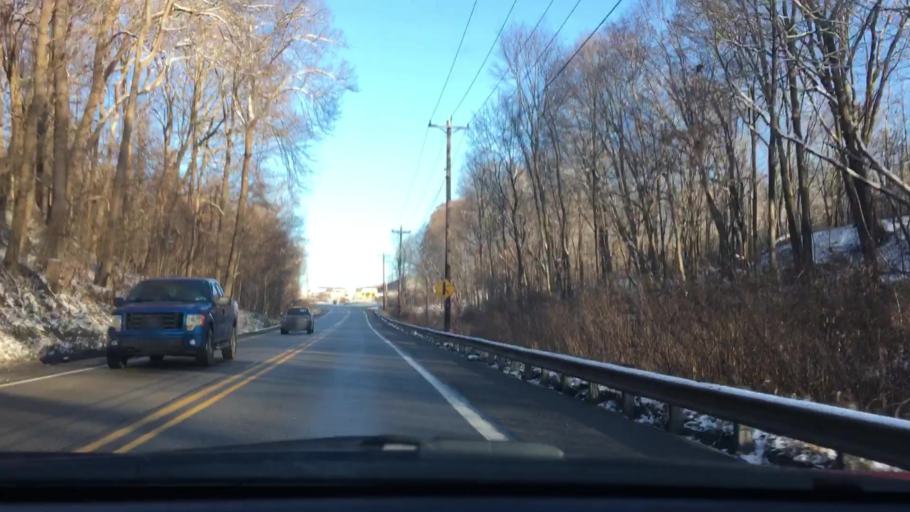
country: US
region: Pennsylvania
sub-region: Allegheny County
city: Glassport
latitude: 40.3344
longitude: -79.9109
